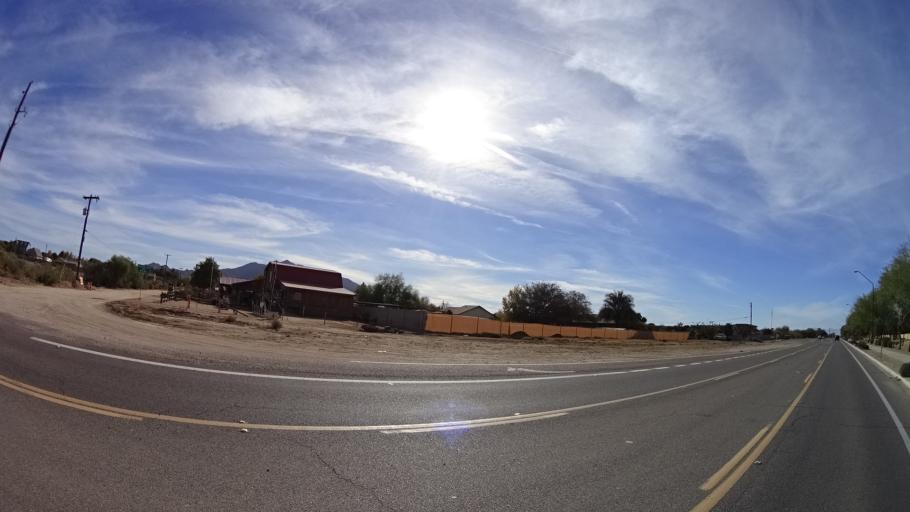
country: US
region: Arizona
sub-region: Maricopa County
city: Queen Creek
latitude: 33.2195
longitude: -111.6989
